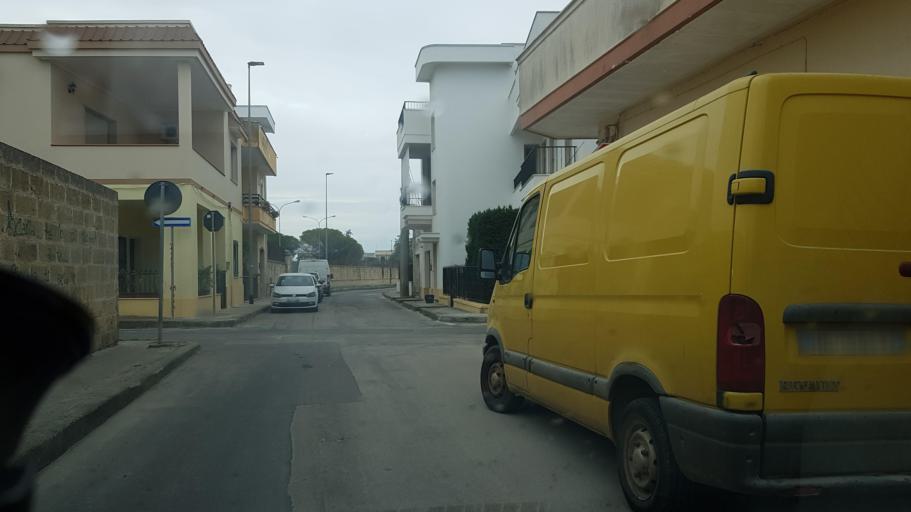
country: IT
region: Apulia
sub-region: Provincia di Lecce
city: Leverano
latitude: 40.2858
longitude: 17.9993
